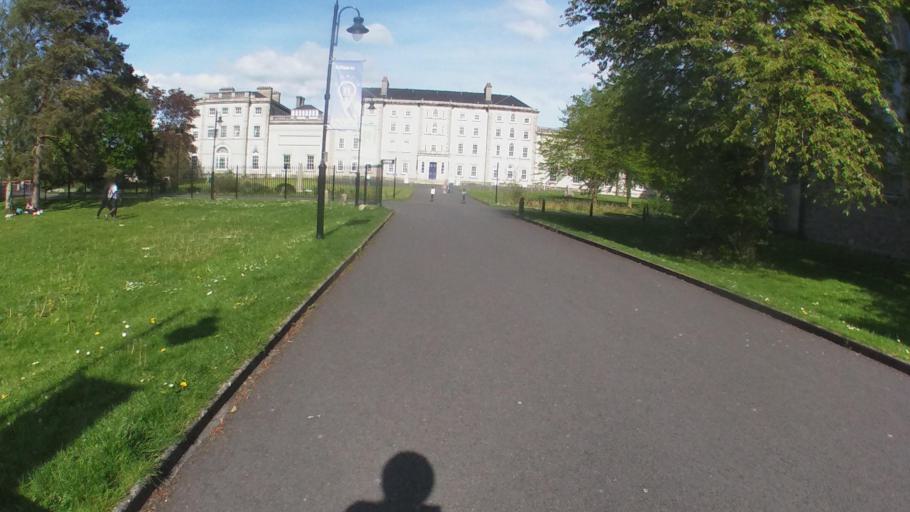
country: IE
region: Leinster
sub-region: County Carlow
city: Carlow
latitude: 52.8373
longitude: -6.9282
